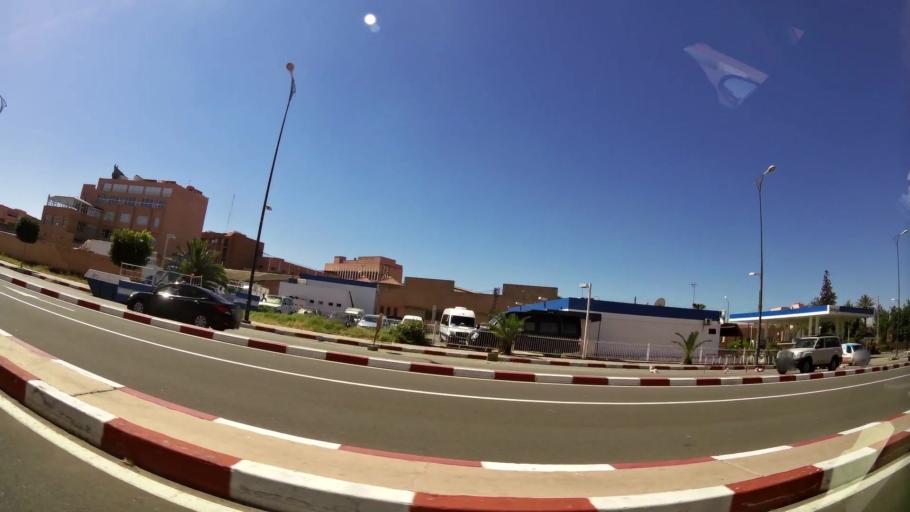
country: MA
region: Marrakech-Tensift-Al Haouz
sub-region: Marrakech
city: Marrakesh
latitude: 31.6269
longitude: -8.0300
